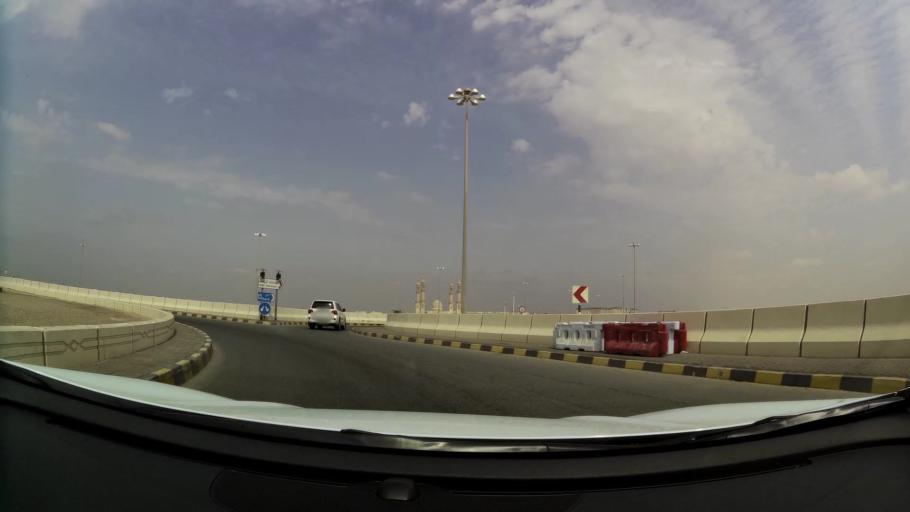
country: AE
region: Abu Dhabi
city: Abu Dhabi
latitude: 24.5106
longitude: 54.6651
